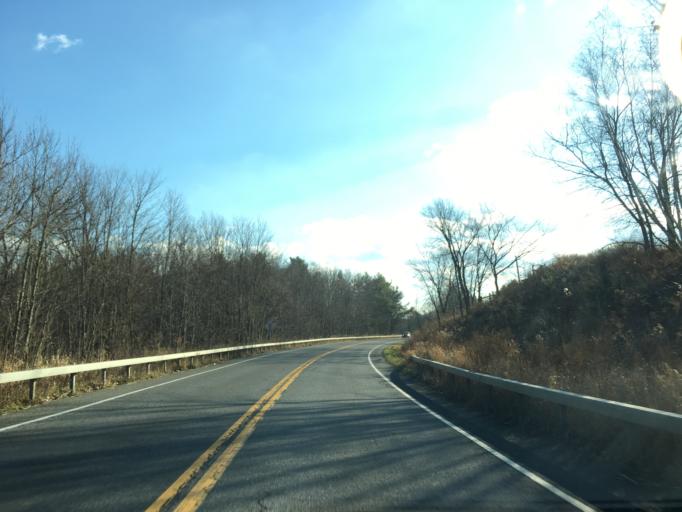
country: US
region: New York
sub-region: Rensselaer County
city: West Sand Lake
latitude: 42.6082
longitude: -73.6179
